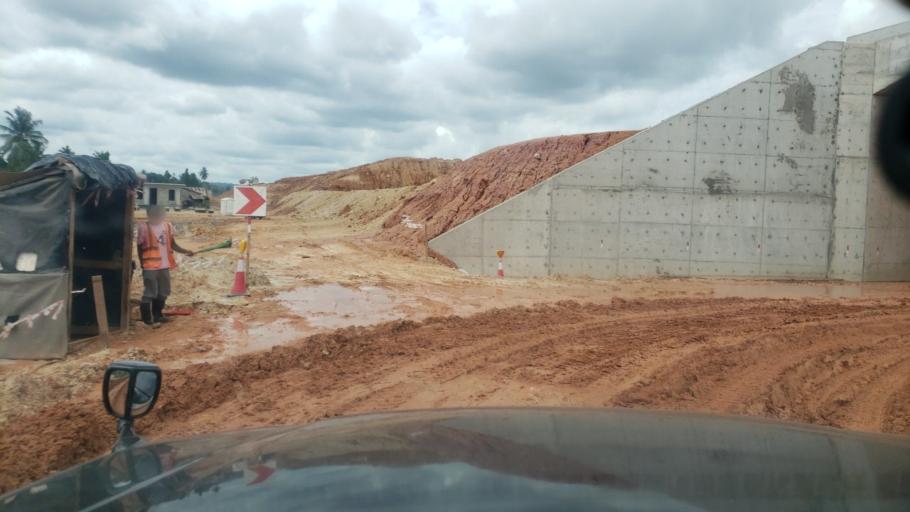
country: TZ
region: Pwani
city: Kisarawe
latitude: -6.8854
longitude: 39.1468
